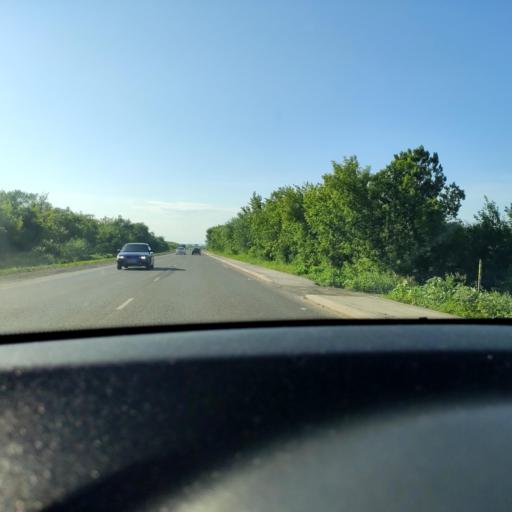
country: RU
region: Samara
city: Samara
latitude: 53.0821
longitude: 50.1621
